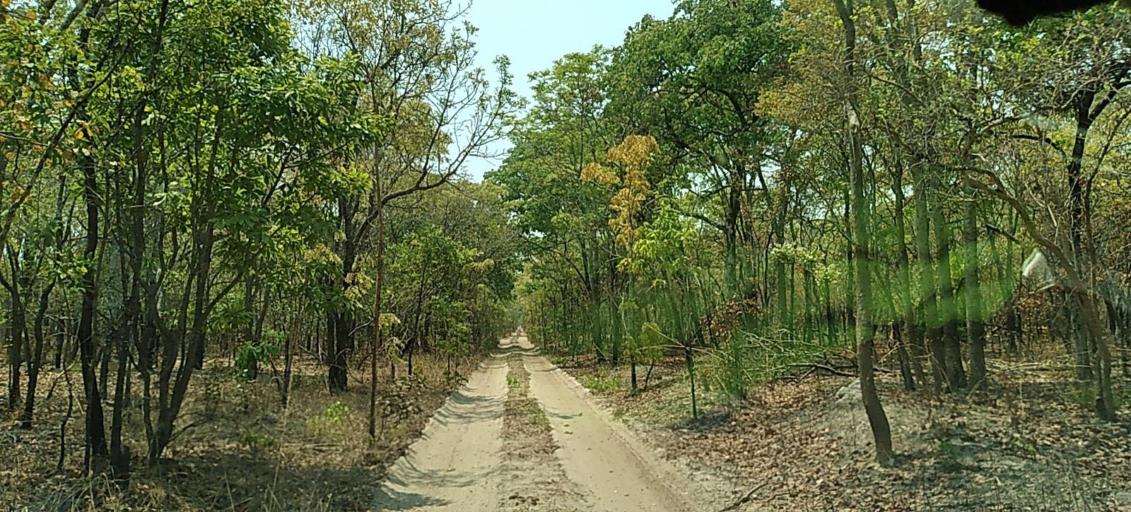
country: ZM
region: North-Western
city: Kabompo
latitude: -13.6572
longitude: 24.4629
